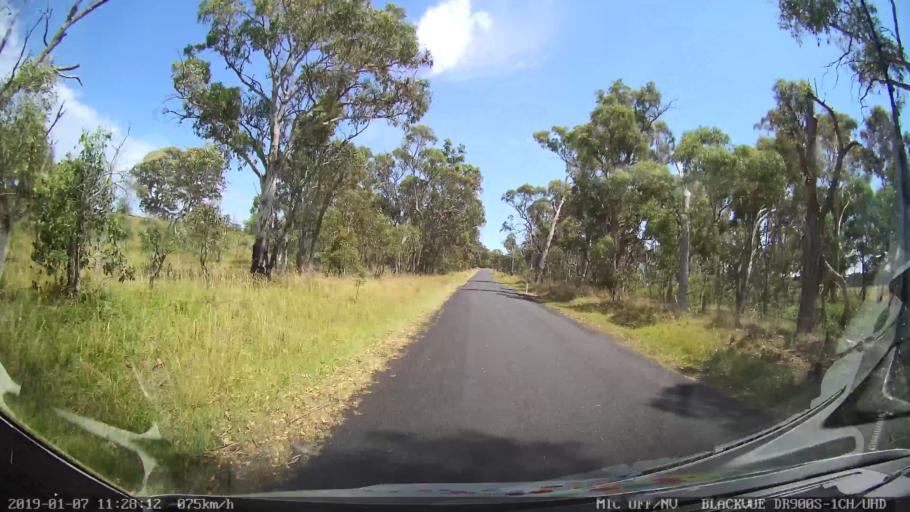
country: AU
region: New South Wales
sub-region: Armidale Dumaresq
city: Armidale
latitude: -30.4509
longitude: 151.5678
